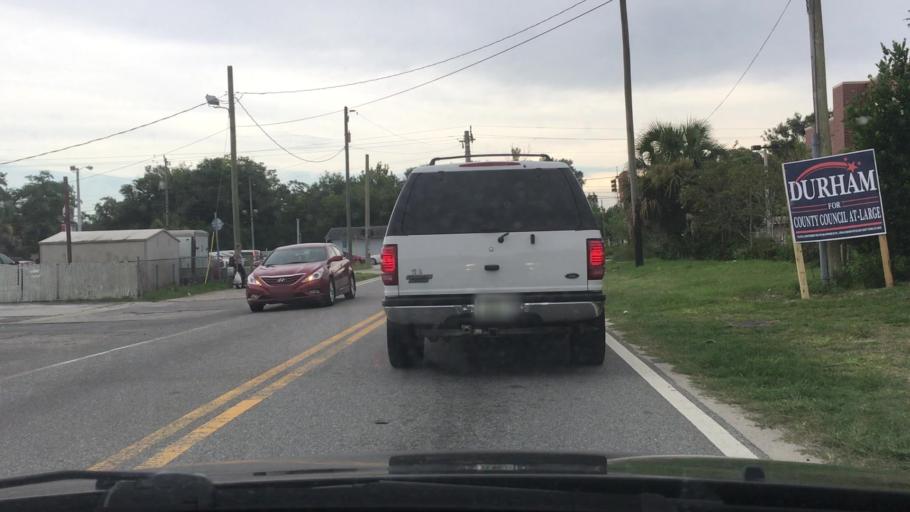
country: US
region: Florida
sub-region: Volusia County
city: Holly Hill
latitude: 29.2169
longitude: -81.0559
